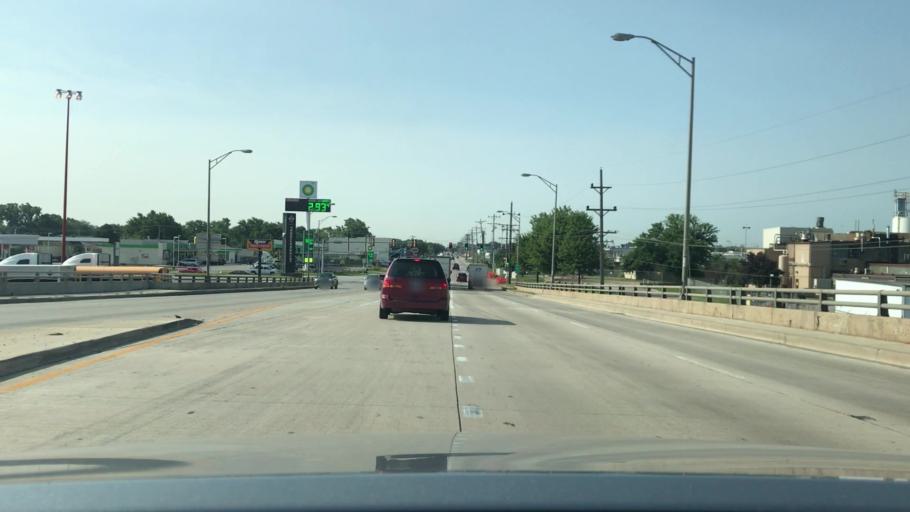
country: US
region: Illinois
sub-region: Cook County
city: Stickney
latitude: 41.8089
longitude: -87.7628
